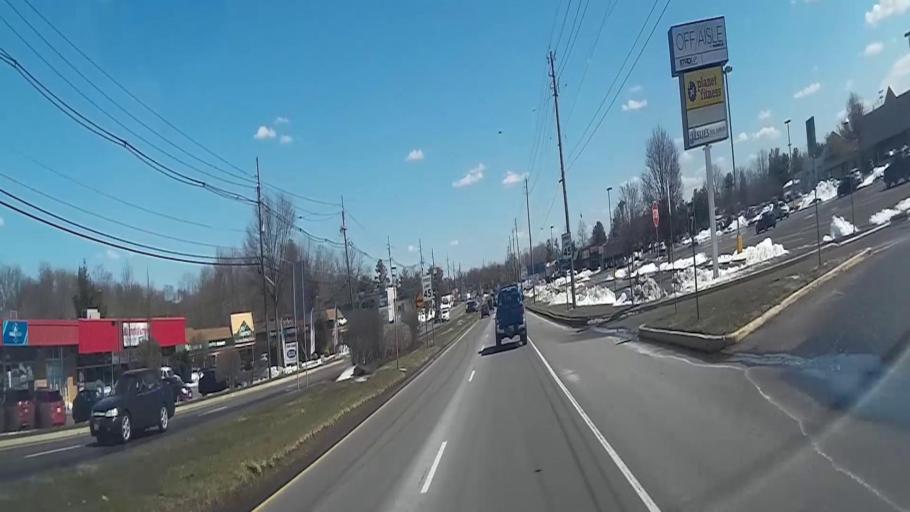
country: US
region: New Jersey
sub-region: Camden County
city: Greentree
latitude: 39.8975
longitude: -74.9518
